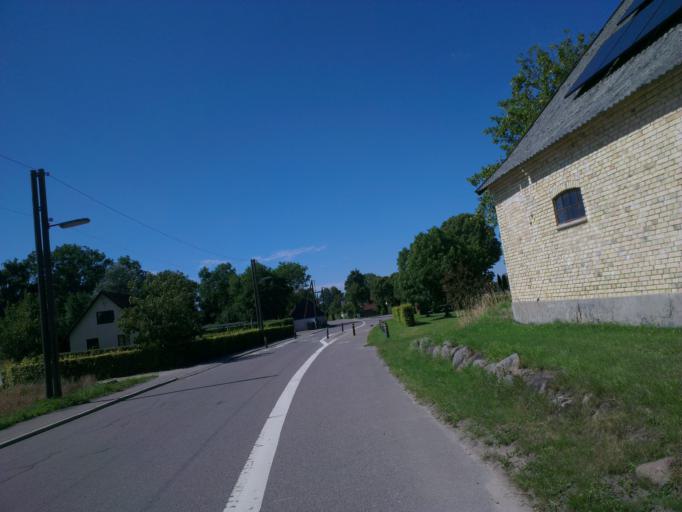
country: DK
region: Capital Region
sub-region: Frederikssund Kommune
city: Frederikssund
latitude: 55.8601
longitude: 12.1011
